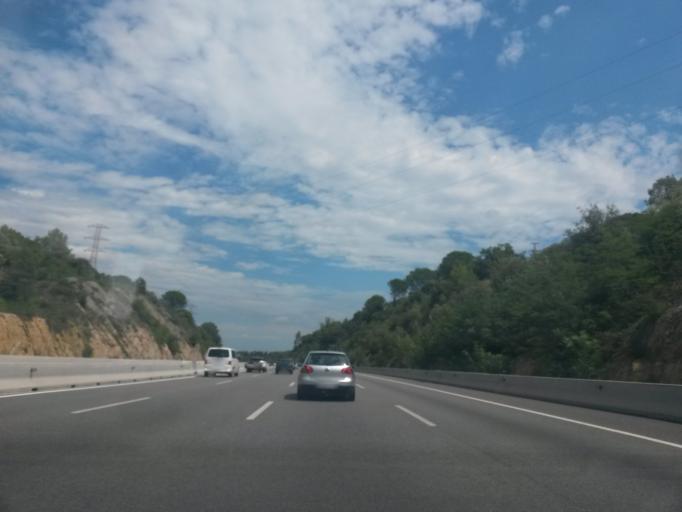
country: ES
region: Catalonia
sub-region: Provincia de Girona
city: Girona
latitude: 42.0015
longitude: 2.8044
